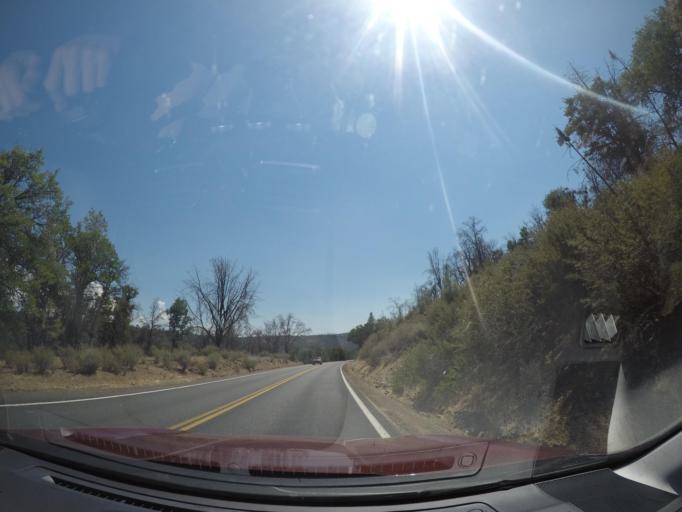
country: US
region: California
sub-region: Shasta County
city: Burney
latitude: 40.9911
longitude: -121.5126
